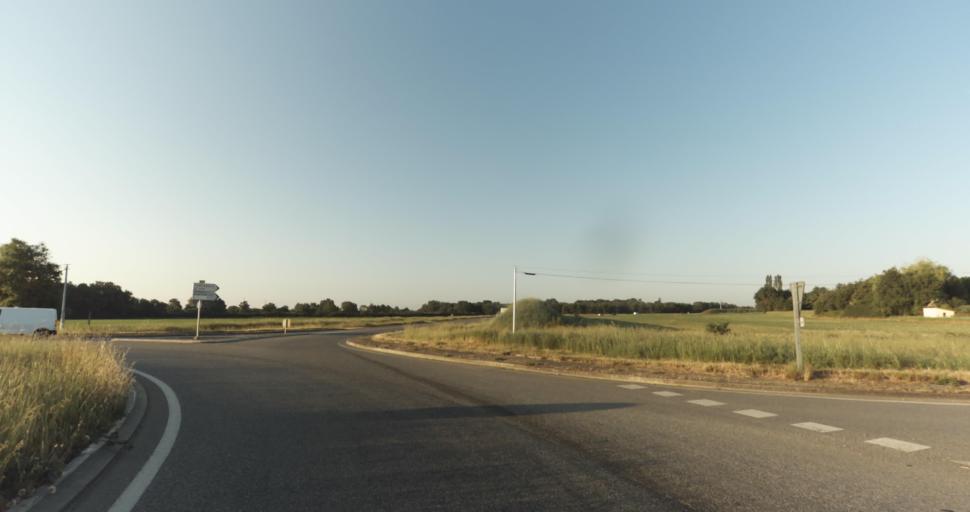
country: FR
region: Midi-Pyrenees
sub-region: Departement de la Haute-Garonne
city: Leguevin
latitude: 43.5806
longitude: 1.2175
